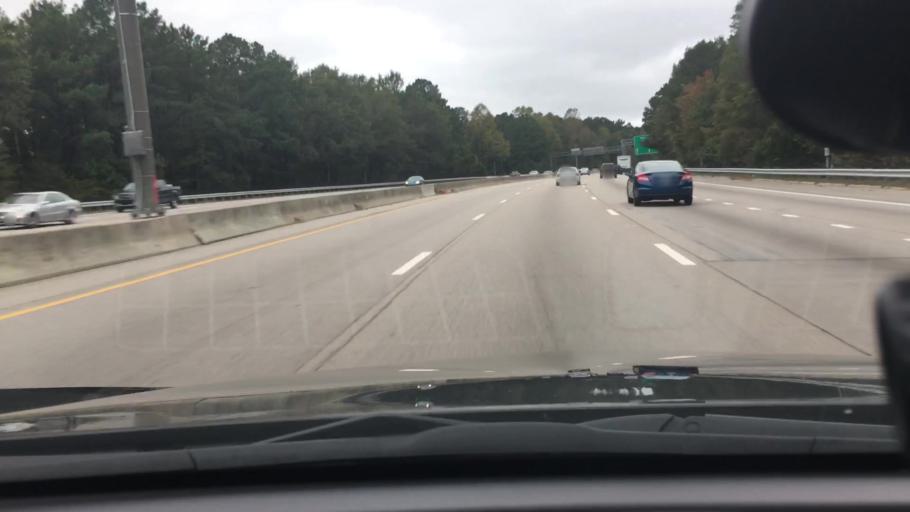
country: US
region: North Carolina
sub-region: Wake County
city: Garner
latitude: 35.7549
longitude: -78.5807
